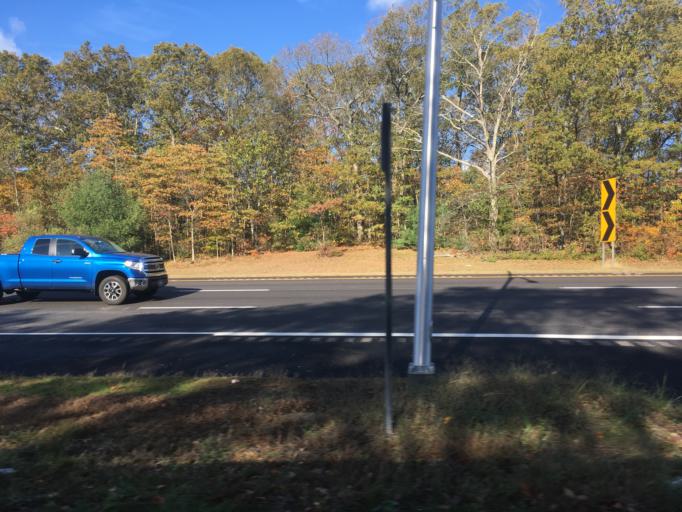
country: US
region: Rhode Island
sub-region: Kent County
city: East Greenwich
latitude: 41.6659
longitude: -71.4893
